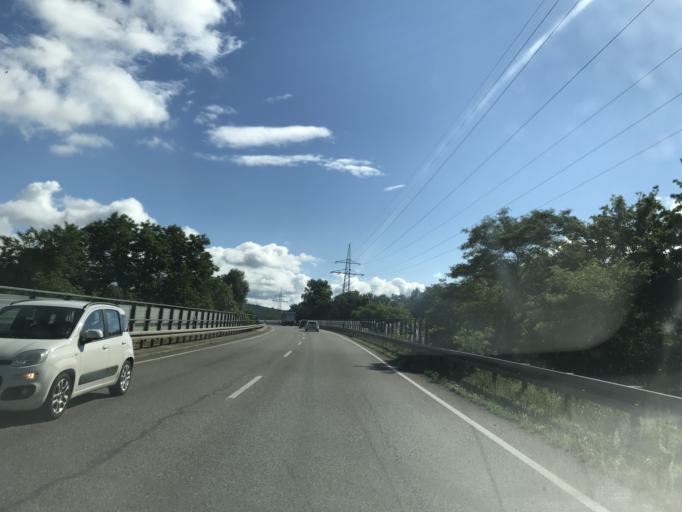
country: DE
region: Baden-Wuerttemberg
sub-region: Freiburg Region
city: Loerrach
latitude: 47.6355
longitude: 7.6870
